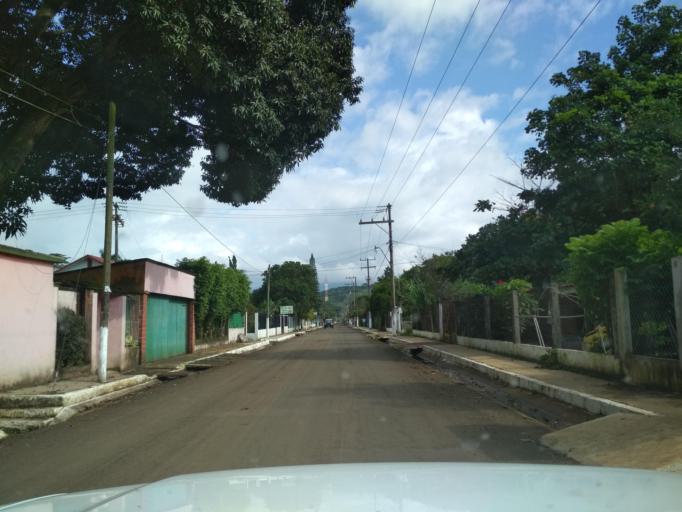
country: MX
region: Veracruz
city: Catemaco
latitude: 18.3770
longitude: -95.1254
